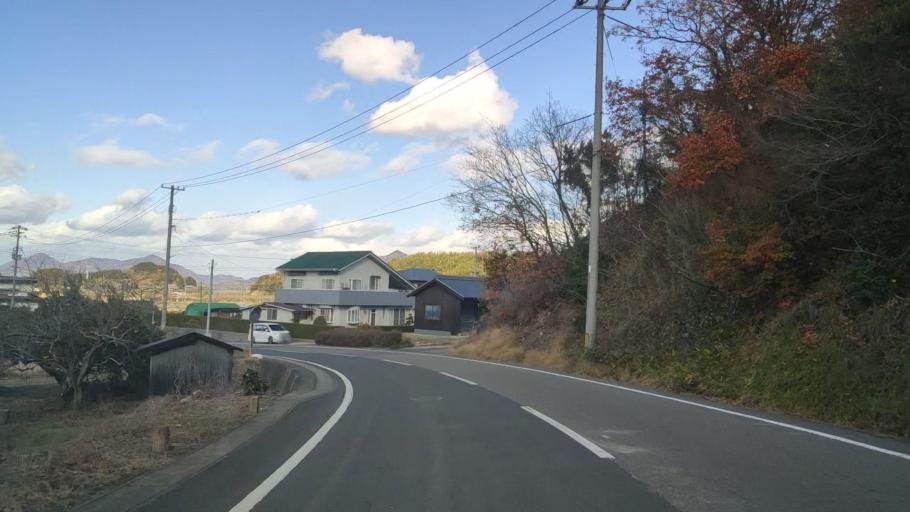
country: JP
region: Hiroshima
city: Innoshima
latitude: 34.2099
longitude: 133.1230
